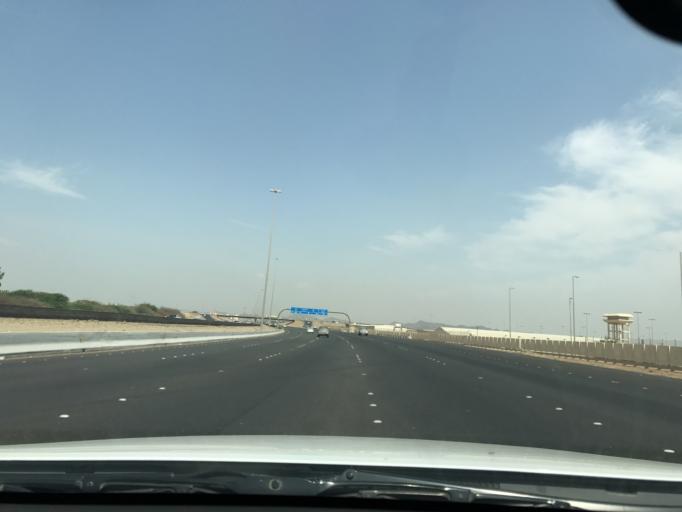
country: SA
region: Makkah
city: Jeddah
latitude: 21.3893
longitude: 39.4186
